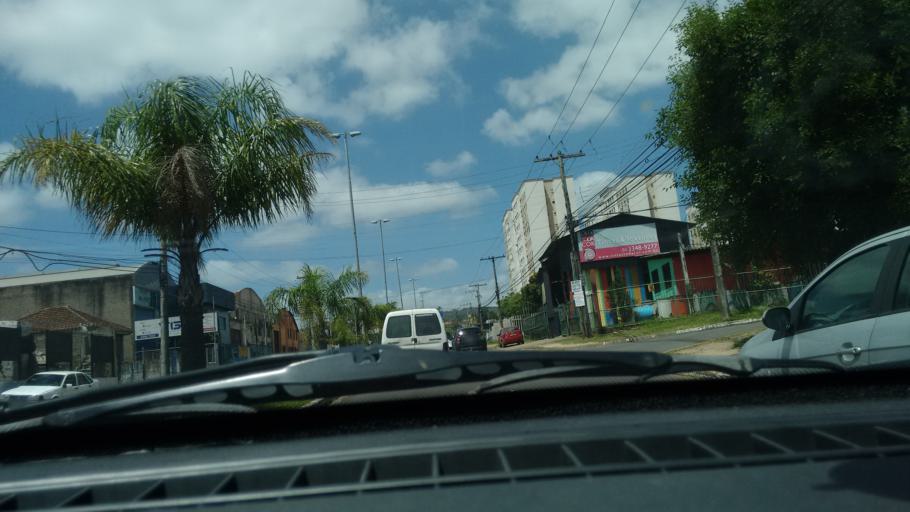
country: BR
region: Rio Grande do Sul
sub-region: Cachoeirinha
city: Cachoeirinha
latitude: -30.0177
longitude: -51.1195
